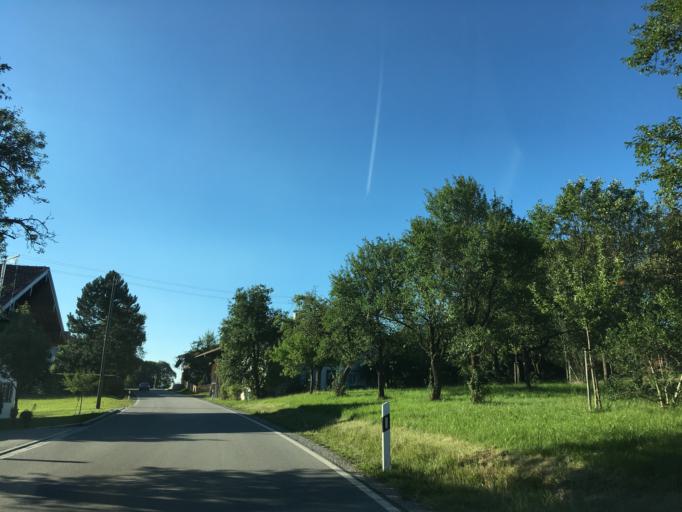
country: DE
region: Bavaria
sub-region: Upper Bavaria
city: Frasdorf
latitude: 47.8279
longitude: 12.2579
